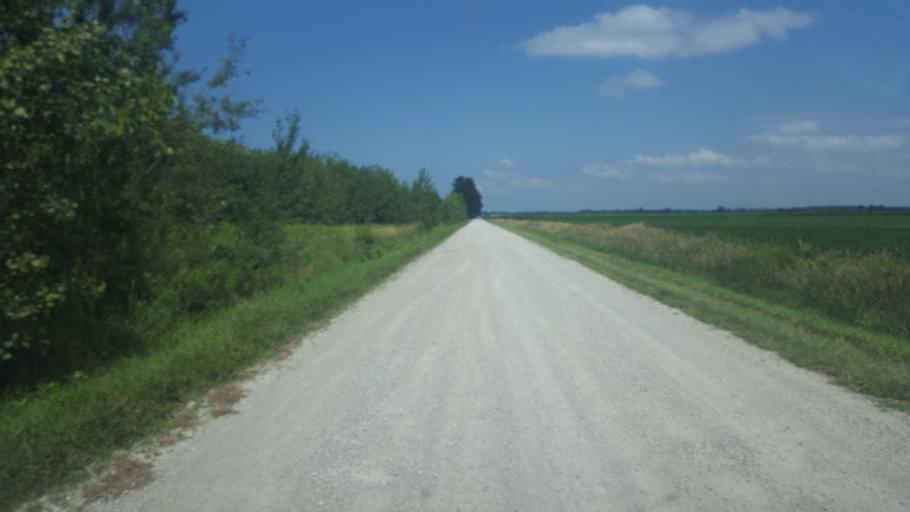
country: US
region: Ohio
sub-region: Huron County
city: Willard
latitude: 40.9959
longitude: -82.7673
